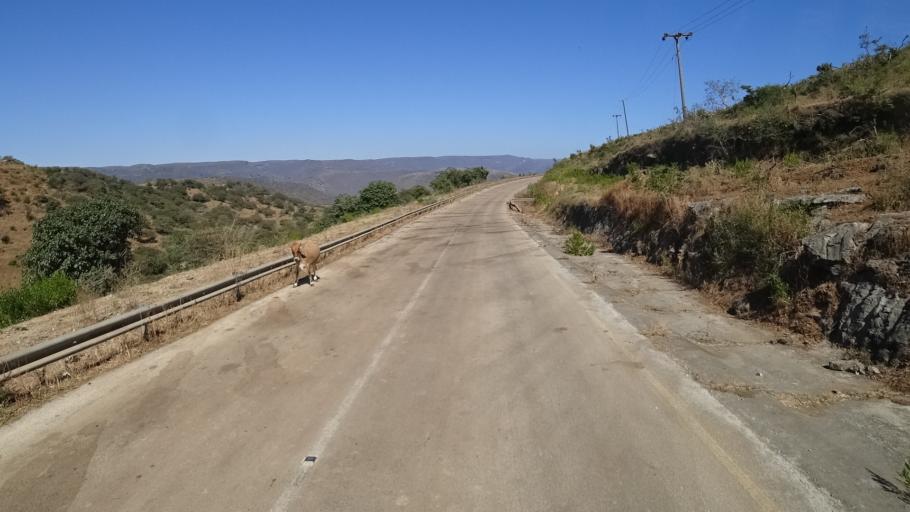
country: YE
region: Al Mahrah
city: Hawf
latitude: 16.7435
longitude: 53.3714
